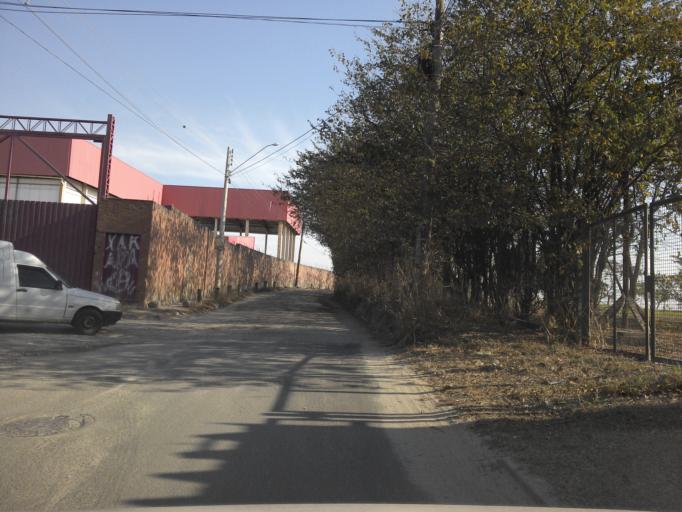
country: BR
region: Sao Paulo
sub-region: Hortolandia
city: Hortolandia
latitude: -22.9111
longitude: -47.2180
